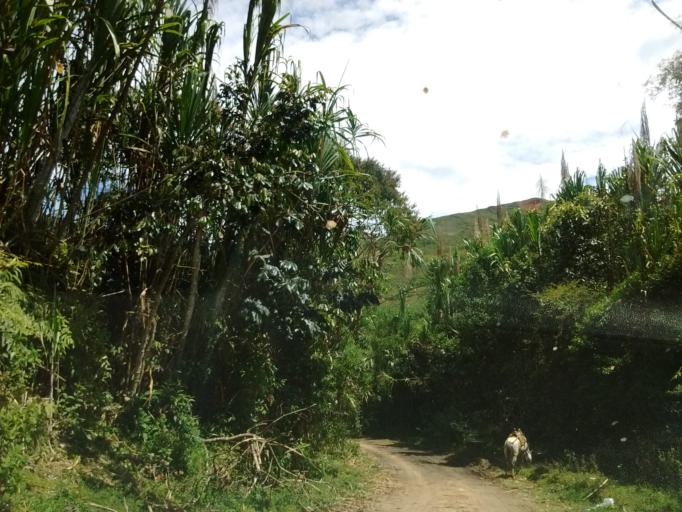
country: CO
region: Cauca
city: Villa Rica
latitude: 2.6541
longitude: -76.7681
